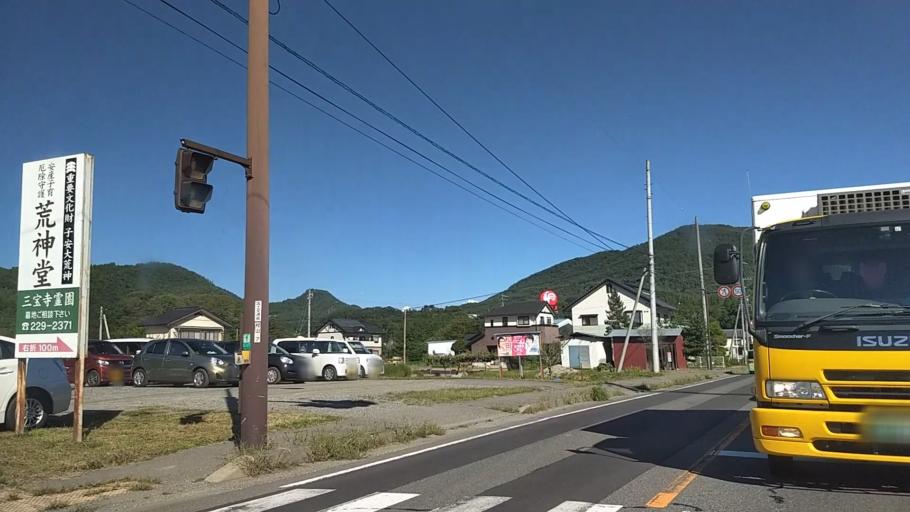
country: JP
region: Nagano
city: Nagano-shi
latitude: 36.6171
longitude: 138.0957
